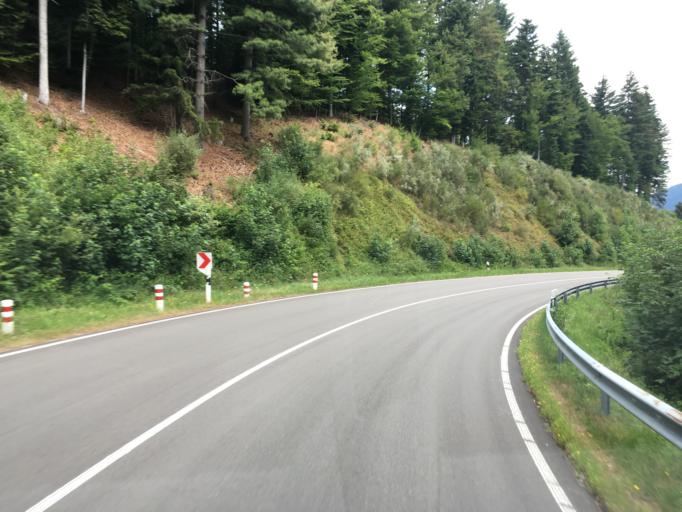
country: DE
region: Baden-Wuerttemberg
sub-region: Karlsruhe Region
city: Baden-Baden
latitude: 48.7134
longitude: 8.2363
